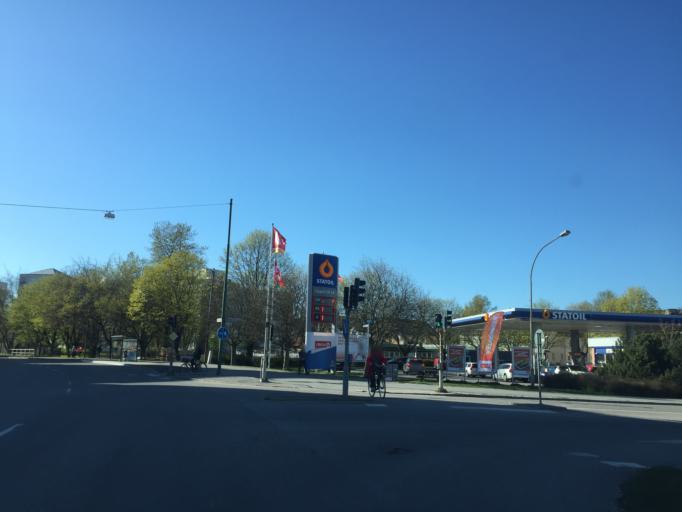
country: SE
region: OErebro
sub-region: Orebro Kommun
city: Orebro
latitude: 59.2660
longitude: 15.2326
